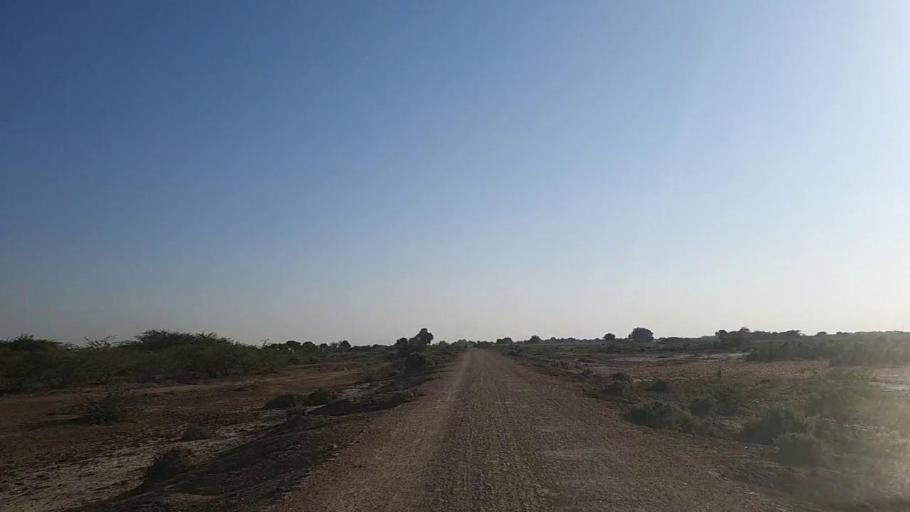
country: PK
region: Sindh
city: Naukot
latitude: 24.9546
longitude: 69.3882
